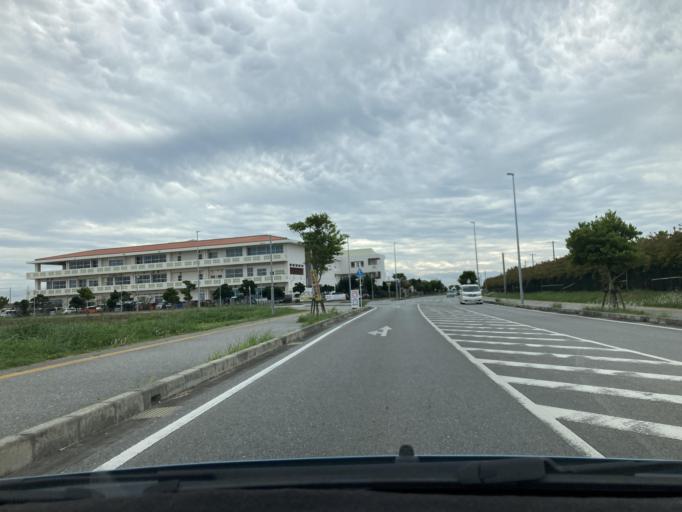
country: JP
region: Okinawa
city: Ishikawa
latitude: 26.3974
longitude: 127.7407
